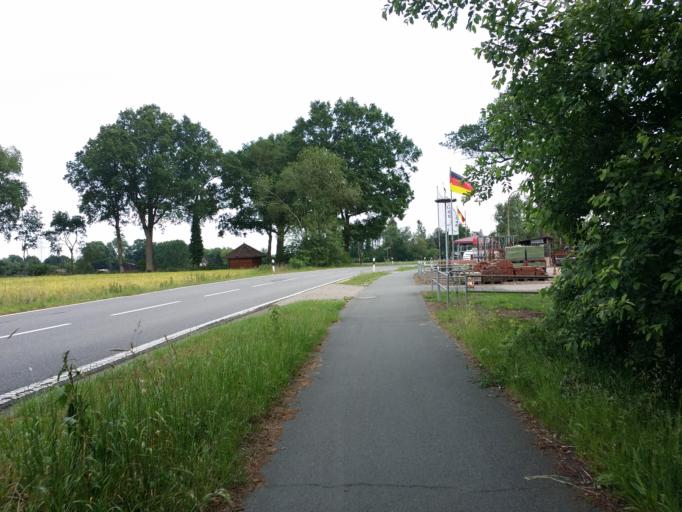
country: DE
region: Lower Saxony
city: Rastede
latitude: 53.2193
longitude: 8.1885
